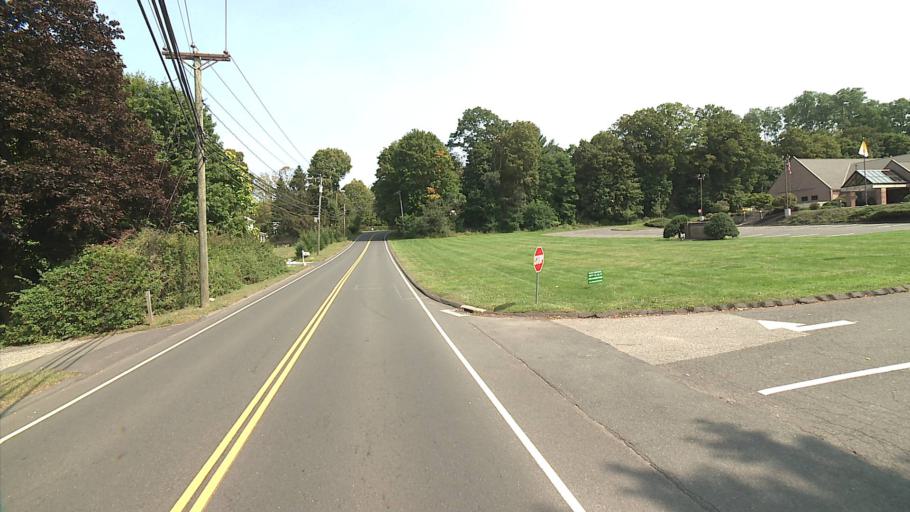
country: US
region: Connecticut
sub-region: Fairfield County
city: Bethel
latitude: 41.3756
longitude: -73.3886
